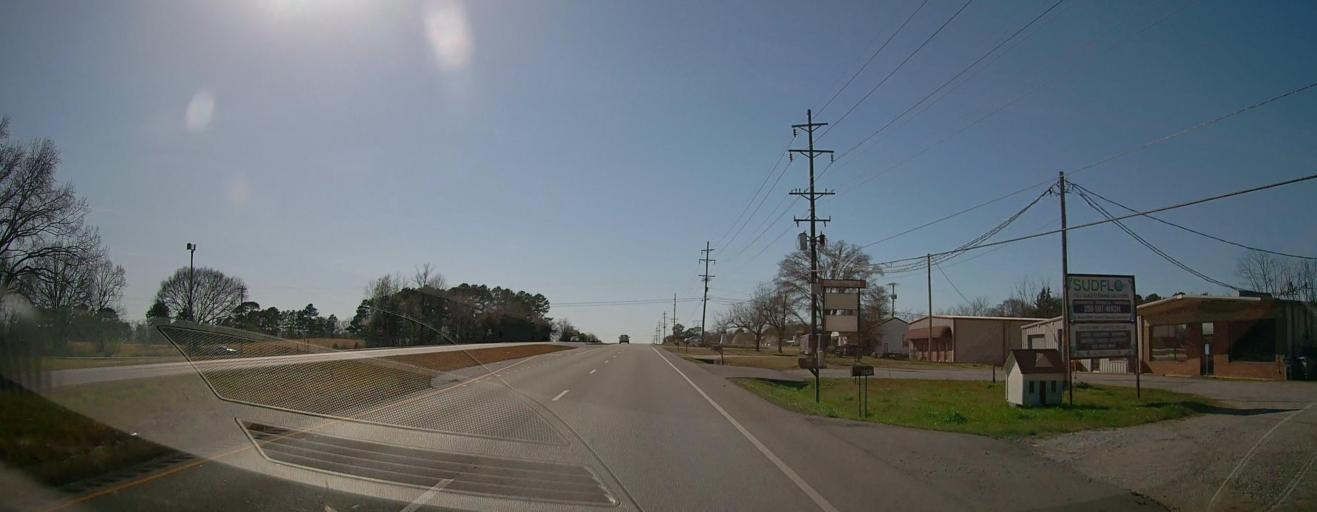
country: US
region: Alabama
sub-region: Lauderdale County
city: Killen
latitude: 34.8598
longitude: -87.4944
